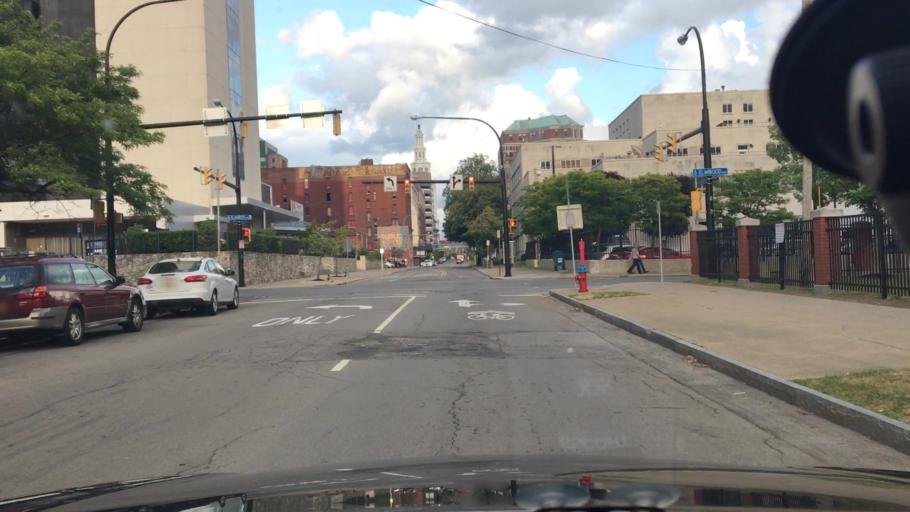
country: US
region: New York
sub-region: Erie County
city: Buffalo
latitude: 42.8896
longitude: -78.8792
